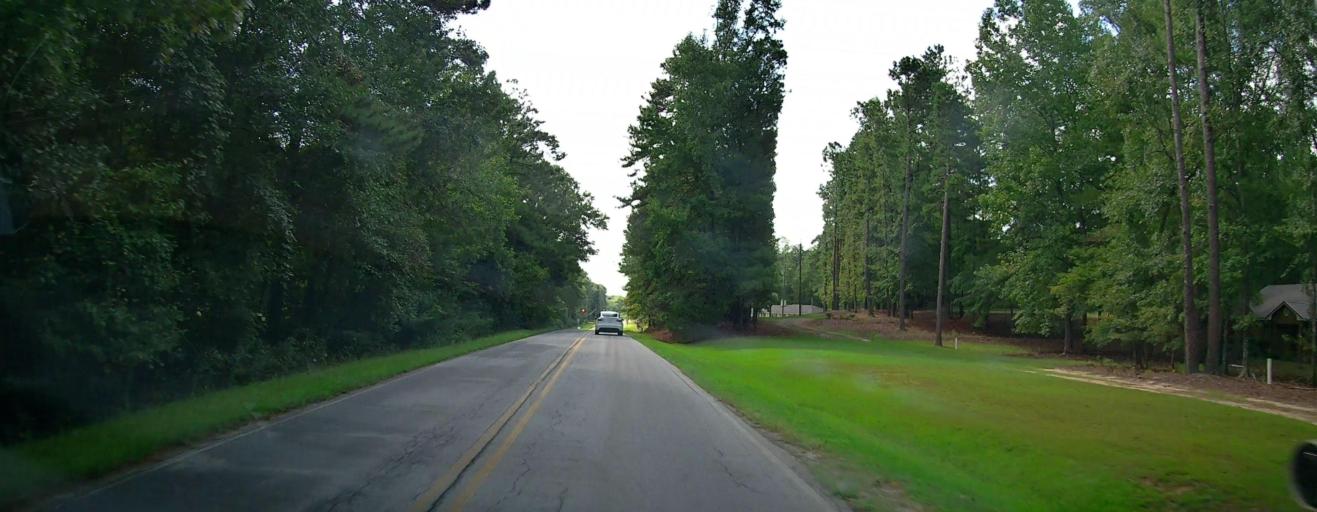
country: US
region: Alabama
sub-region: Russell County
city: Phenix City
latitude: 32.5928
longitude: -84.9389
